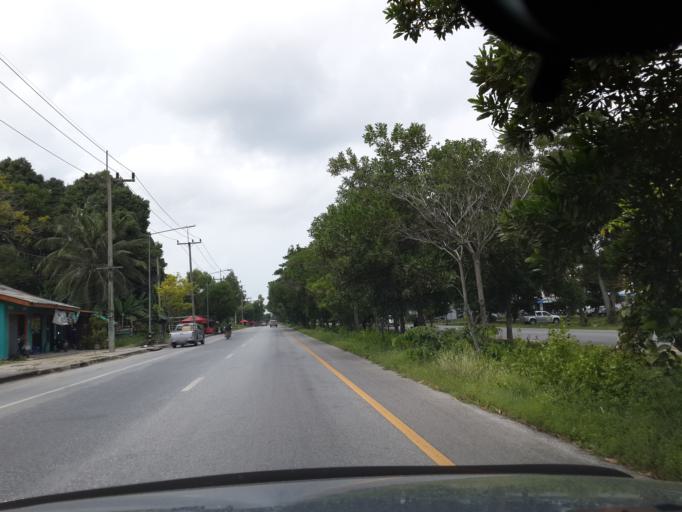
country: TH
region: Pattani
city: Yaring
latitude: 6.8625
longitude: 101.3662
